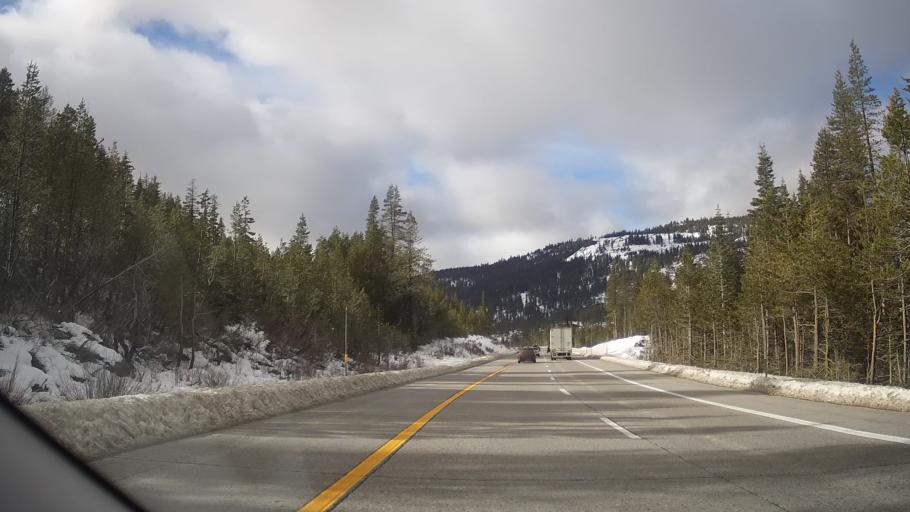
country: US
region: California
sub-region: Nevada County
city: Truckee
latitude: 39.3230
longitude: -120.4085
